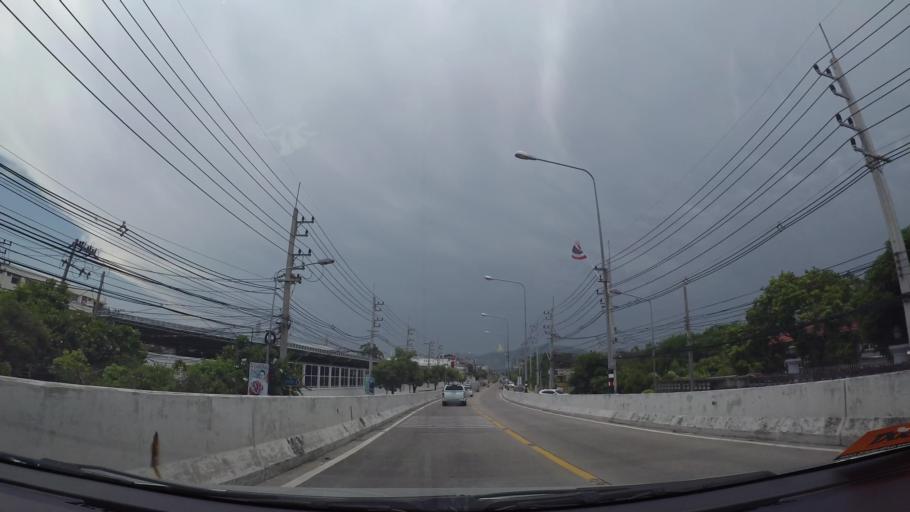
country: TH
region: Chon Buri
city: Chon Buri
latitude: 13.3486
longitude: 100.9814
